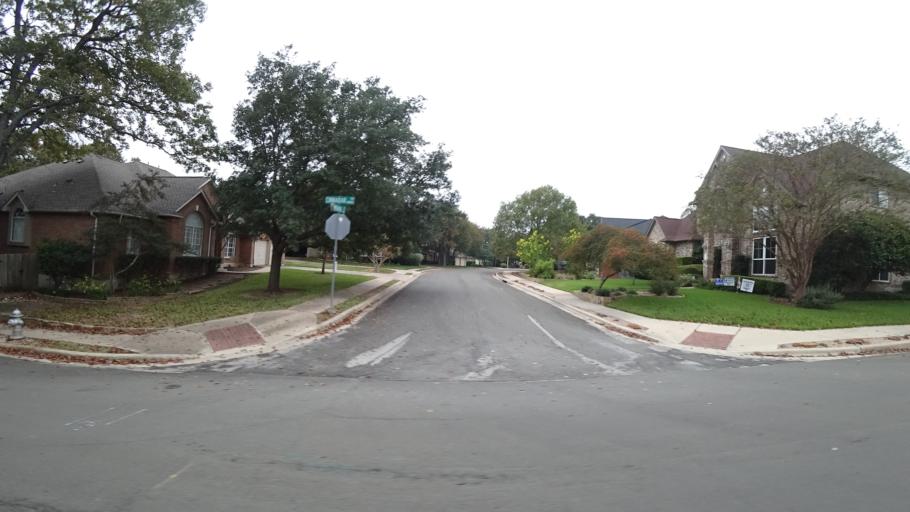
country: US
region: Texas
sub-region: Williamson County
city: Anderson Mill
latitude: 30.4333
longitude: -97.8270
